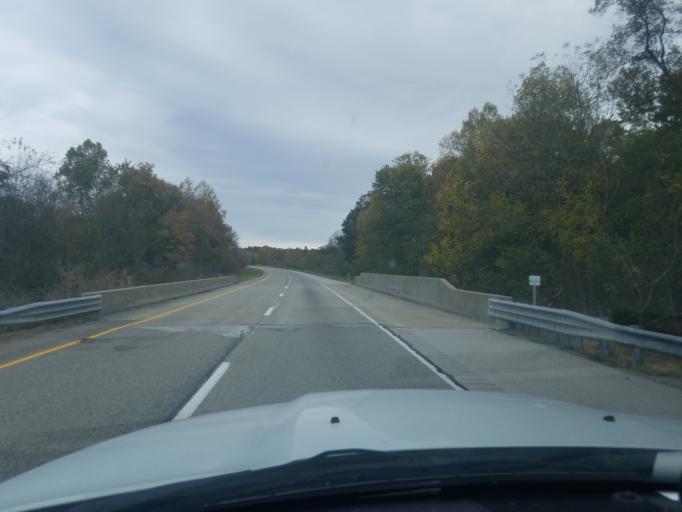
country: US
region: Indiana
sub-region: Spencer County
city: Dale
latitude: 38.1964
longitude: -87.1414
